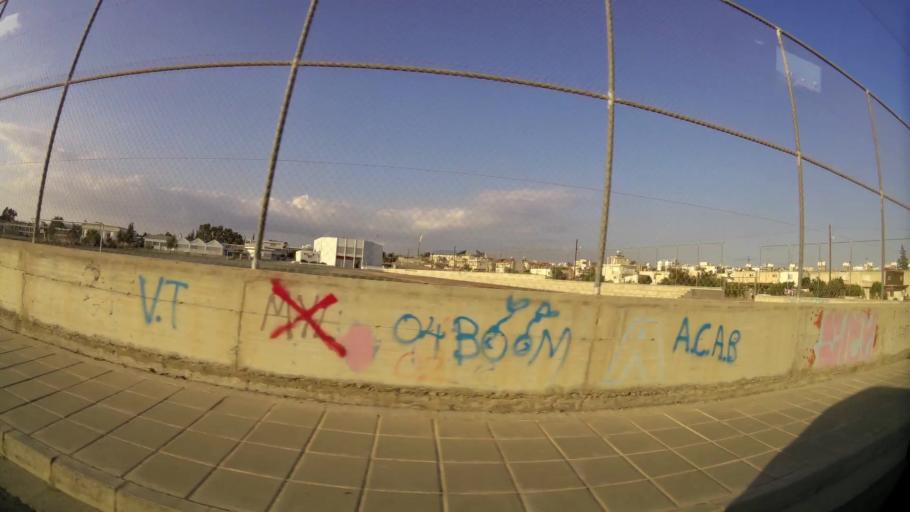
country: CY
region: Larnaka
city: Larnaca
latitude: 34.9178
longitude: 33.5966
